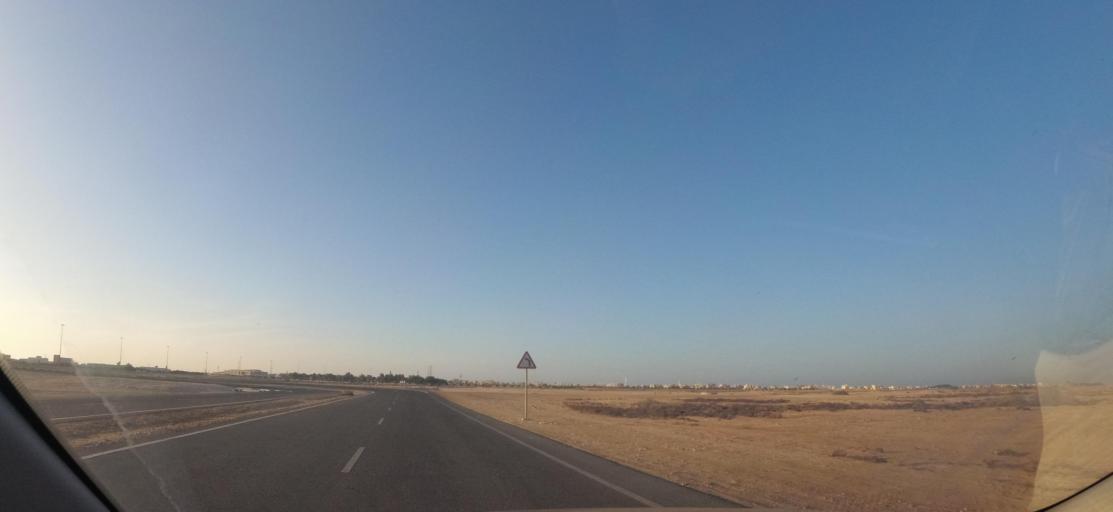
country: QA
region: Madinat ash Shamal
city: Ar Ru'ays
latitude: 26.1189
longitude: 51.2176
